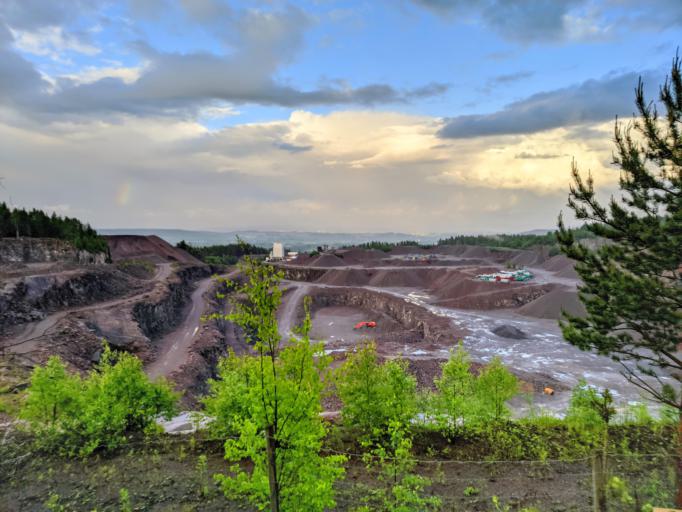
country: NO
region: Akershus
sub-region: Nittedal
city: Rotnes
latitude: 60.0066
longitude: 10.8966
